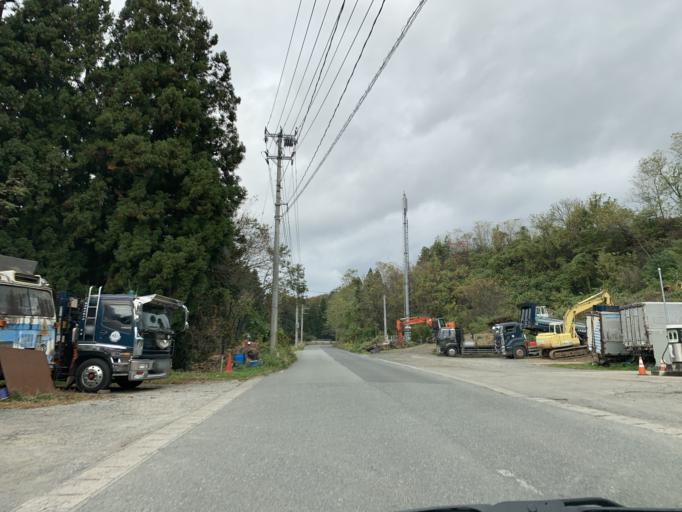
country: JP
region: Iwate
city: Mizusawa
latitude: 39.0489
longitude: 141.1133
